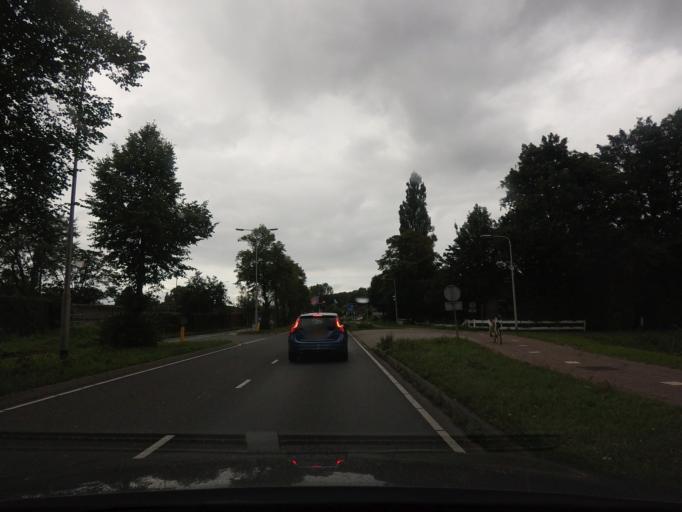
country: NL
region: South Holland
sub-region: Gemeente Leidschendam-Voorburg
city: Voorburg
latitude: 52.1040
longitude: 4.3612
